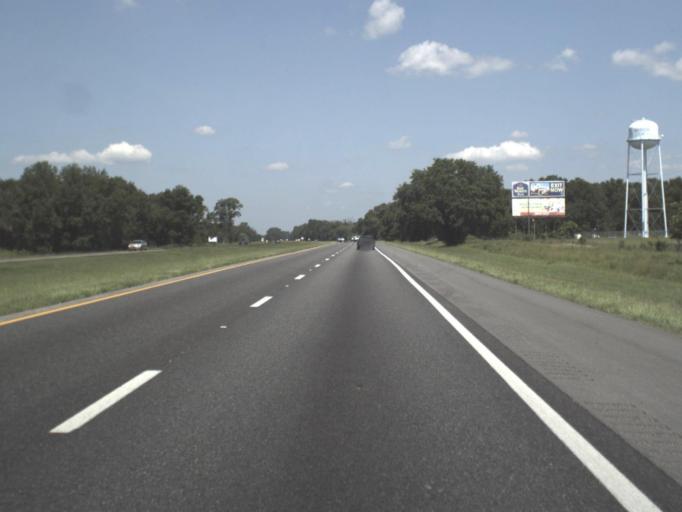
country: US
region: Florida
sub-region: Madison County
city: Madison
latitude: 30.3861
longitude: -83.3182
